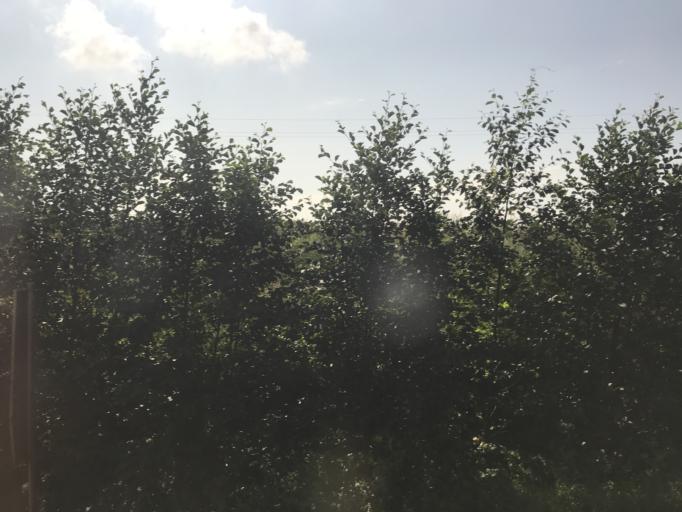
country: PL
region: Kujawsko-Pomorskie
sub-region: Powiat swiecki
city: Bukowiec
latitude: 53.3886
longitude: 18.3207
